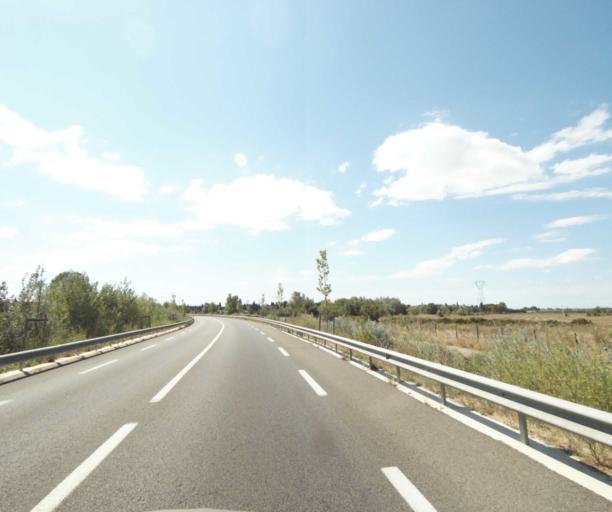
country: FR
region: Languedoc-Roussillon
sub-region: Departement du Gard
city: Rodilhan
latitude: 43.8140
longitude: 4.4127
